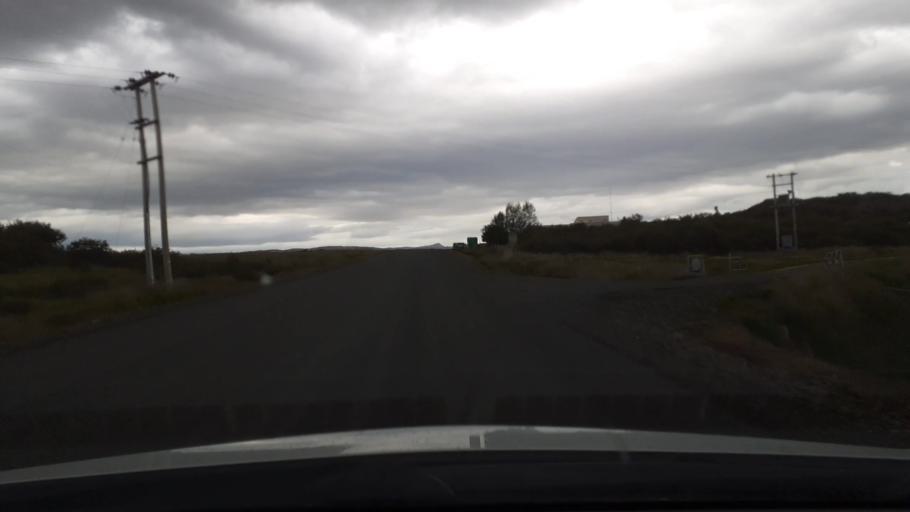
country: IS
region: West
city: Borgarnes
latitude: 64.6726
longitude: -21.7036
